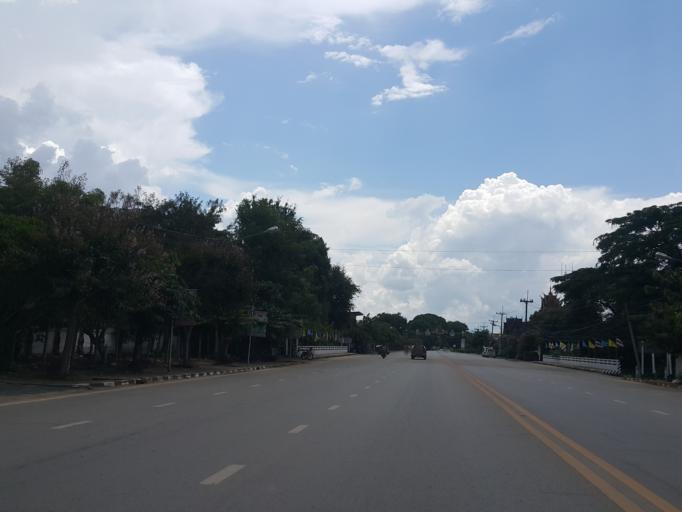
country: TH
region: Chiang Mai
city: Phrao
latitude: 19.3637
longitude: 99.2015
